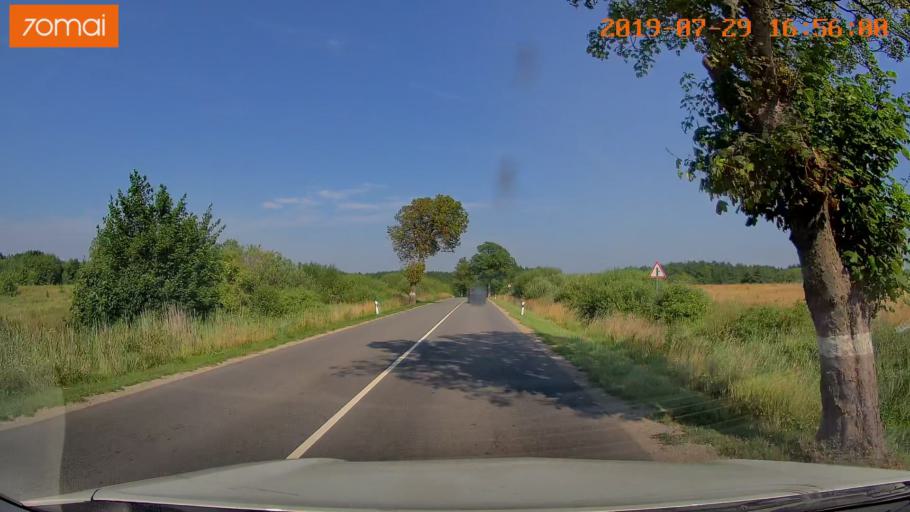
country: RU
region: Kaliningrad
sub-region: Gorod Svetlogorsk
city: Svetlogorsk
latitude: 54.8145
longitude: 20.1615
